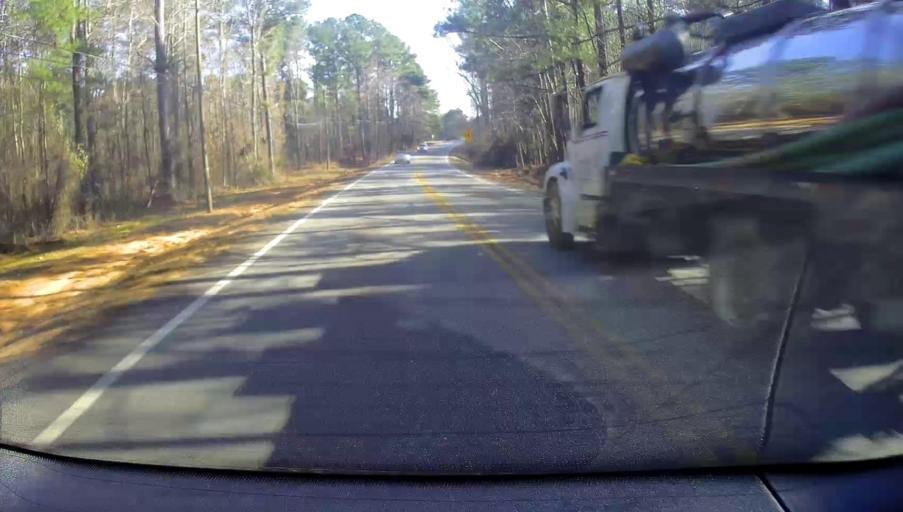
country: US
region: Georgia
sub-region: Butts County
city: Indian Springs
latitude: 33.2767
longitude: -83.9176
